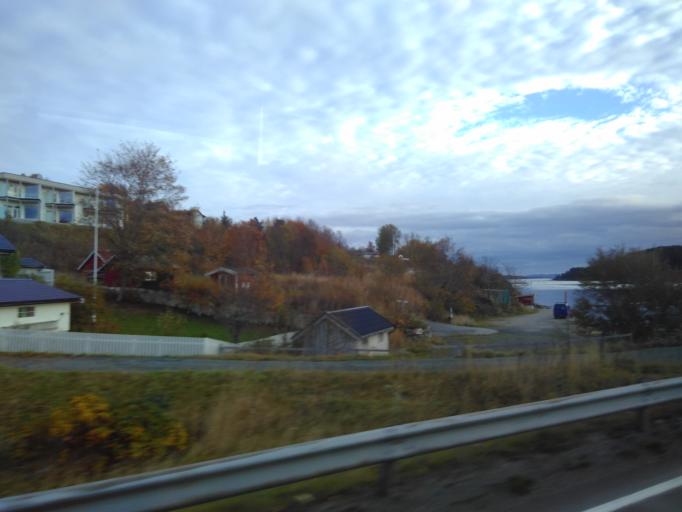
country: NO
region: Sor-Trondelag
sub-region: Hitra
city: Fillan
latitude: 63.5226
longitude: 9.1023
